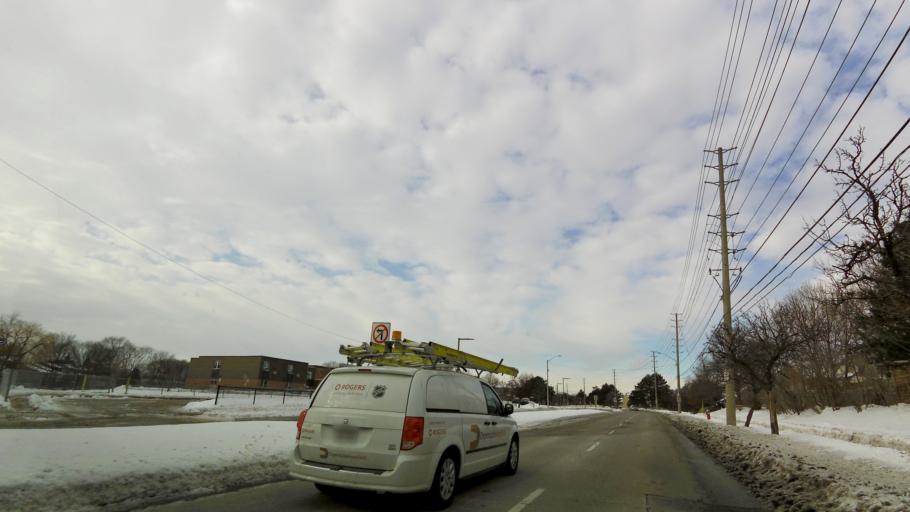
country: CA
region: Ontario
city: Mississauga
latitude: 43.5454
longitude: -79.6948
